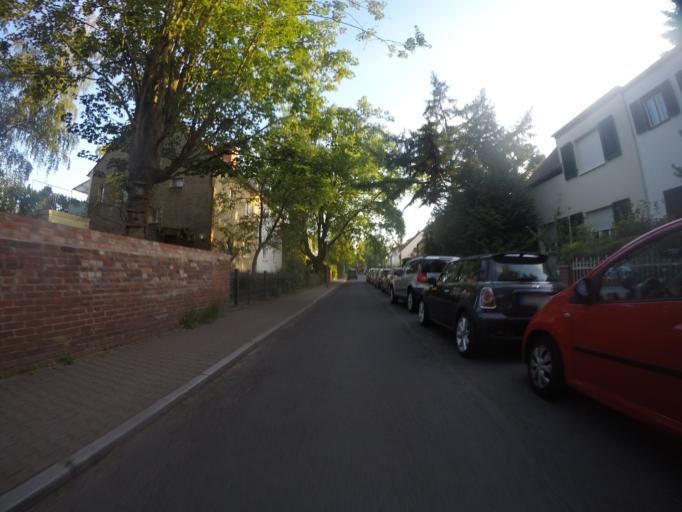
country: DE
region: Berlin
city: Grunewald
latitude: 52.4983
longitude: 13.2673
